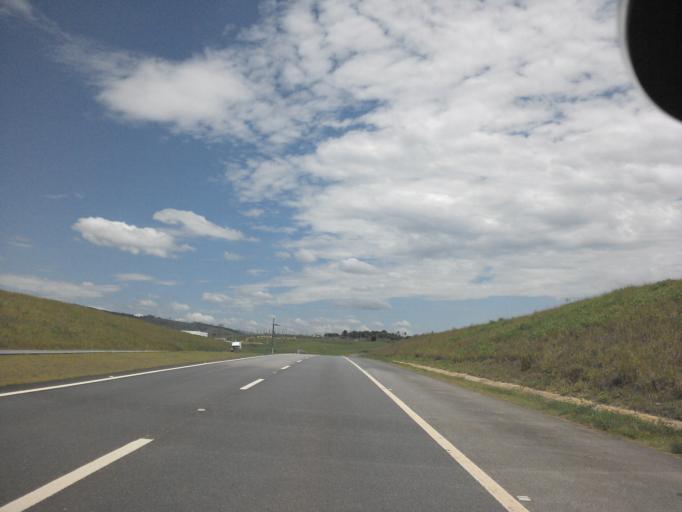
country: BR
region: Sao Paulo
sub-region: Taubate
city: Taubate
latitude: -23.0891
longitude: -45.5683
